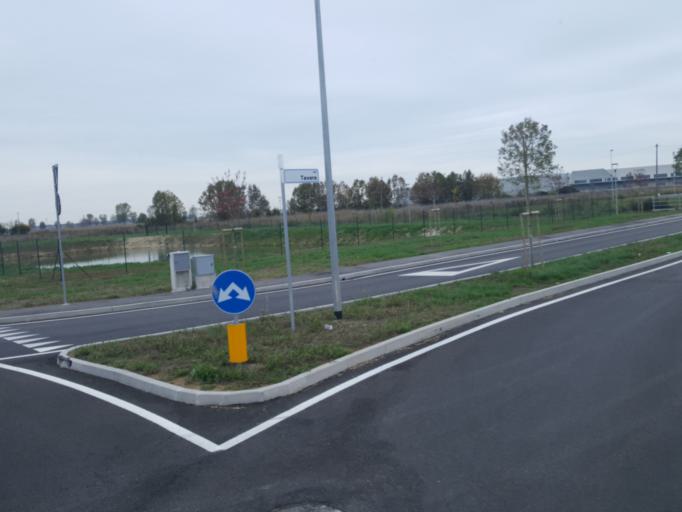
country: IT
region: Veneto
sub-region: Provincia di Verona
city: Pradelle
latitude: 45.2728
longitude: 10.8678
